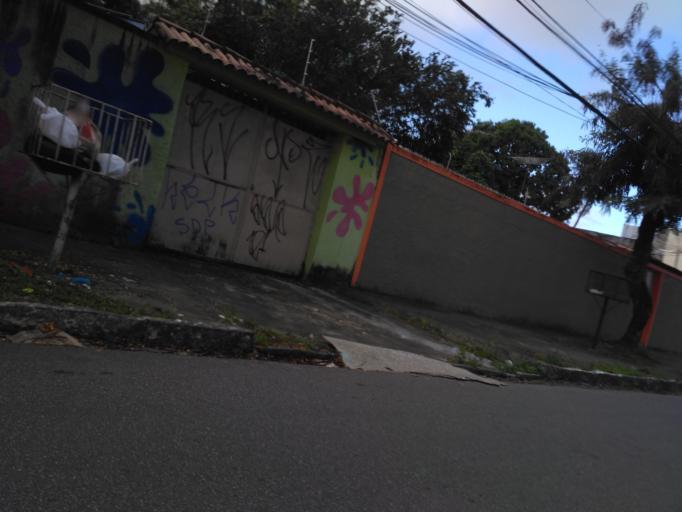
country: BR
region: Pernambuco
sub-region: Recife
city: Recife
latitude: -8.0516
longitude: -34.9411
